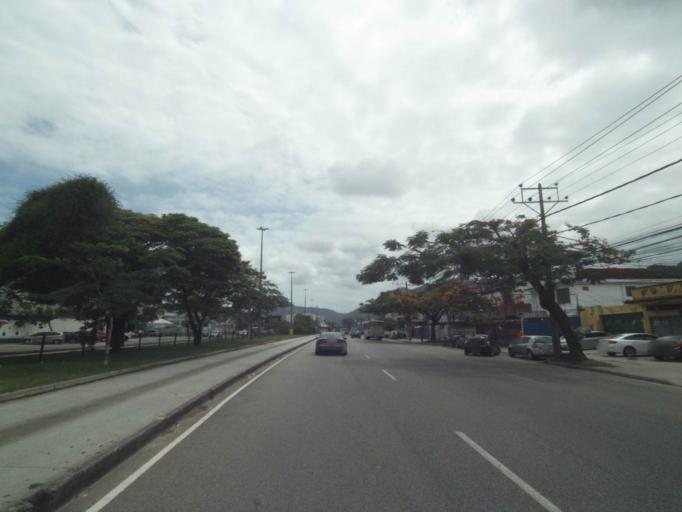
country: BR
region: Rio de Janeiro
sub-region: Nilopolis
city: Nilopolis
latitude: -22.9592
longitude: -43.3864
